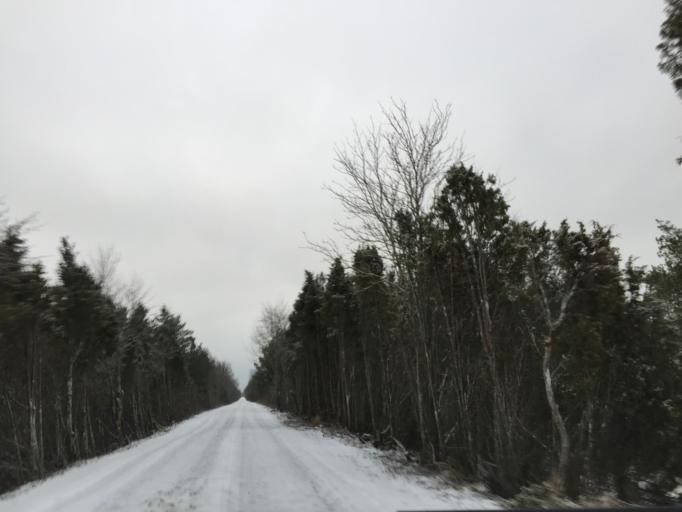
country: EE
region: Saare
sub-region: Orissaare vald
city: Orissaare
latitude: 58.5613
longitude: 23.3876
